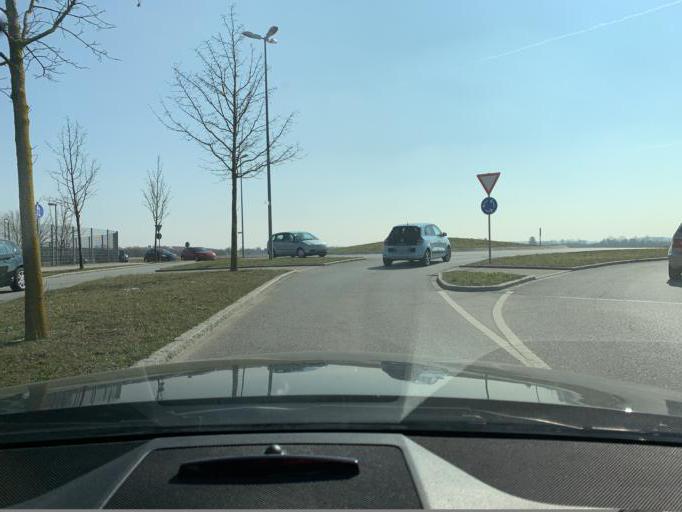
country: DE
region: Bavaria
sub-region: Upper Bavaria
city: Erding
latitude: 48.3063
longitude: 11.8885
